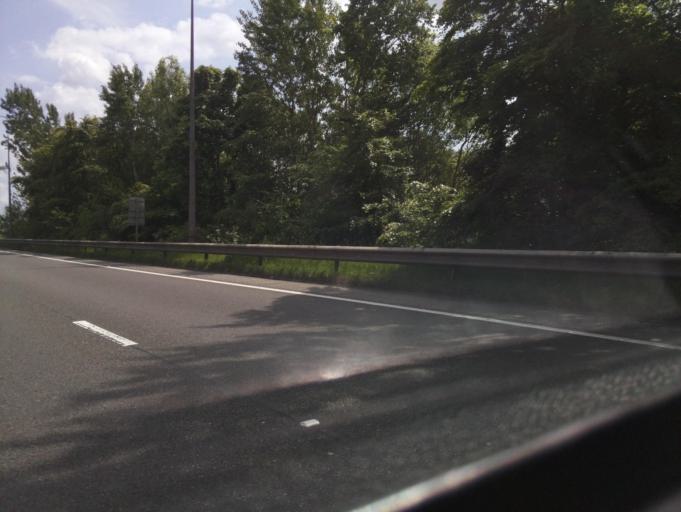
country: GB
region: England
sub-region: County Durham
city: Wingate
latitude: 54.7342
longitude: -1.3585
